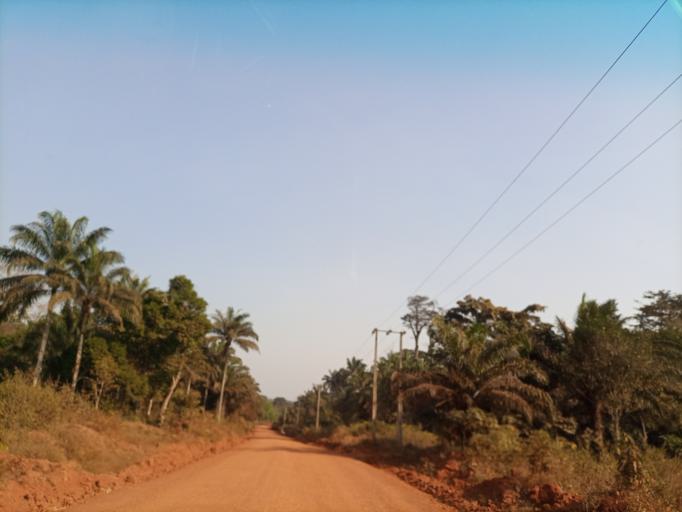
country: NG
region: Enugu
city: Opi
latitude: 6.7604
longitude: 7.3991
